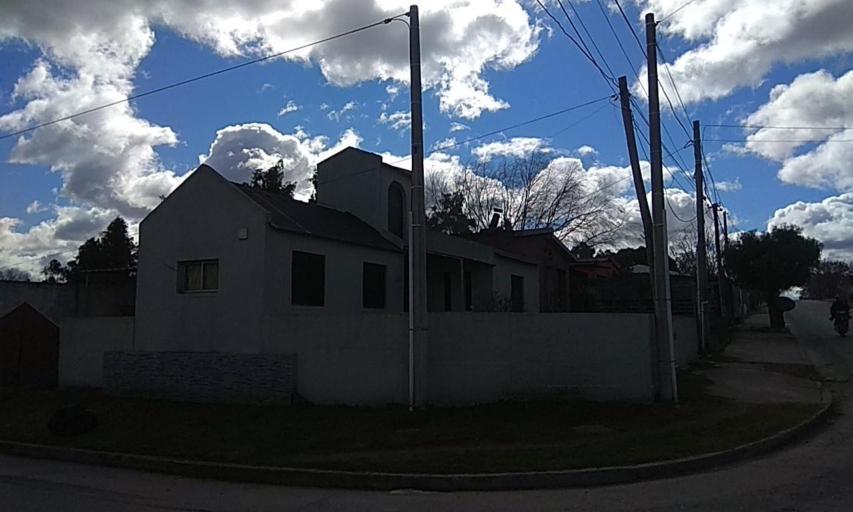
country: UY
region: Florida
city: Florida
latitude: -34.0877
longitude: -56.2259
